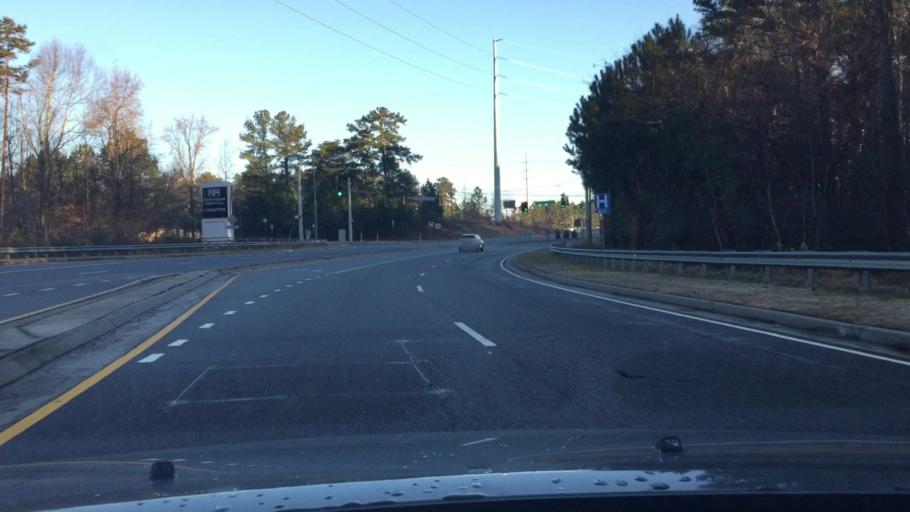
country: US
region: Georgia
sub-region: Forsyth County
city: Cumming
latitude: 34.1775
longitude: -84.1370
